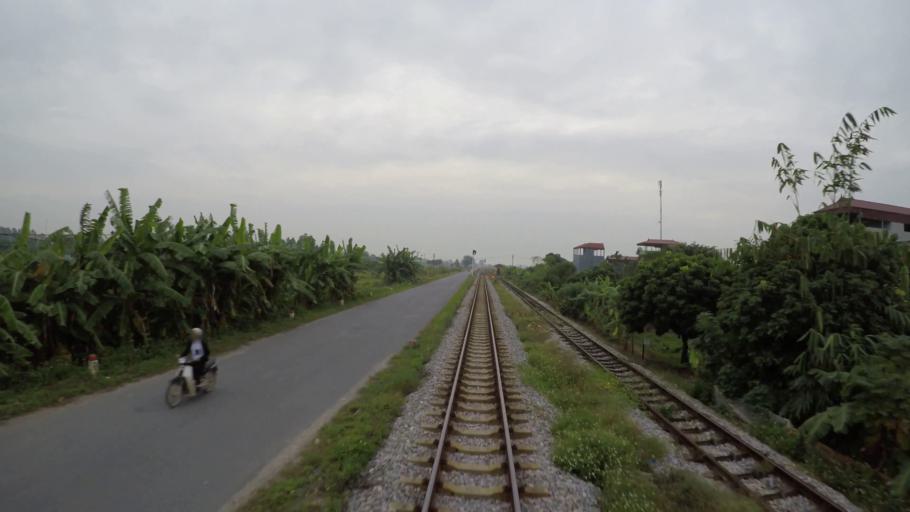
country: VN
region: Hung Yen
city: Ban Yen Nhan
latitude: 20.9724
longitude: 106.0968
